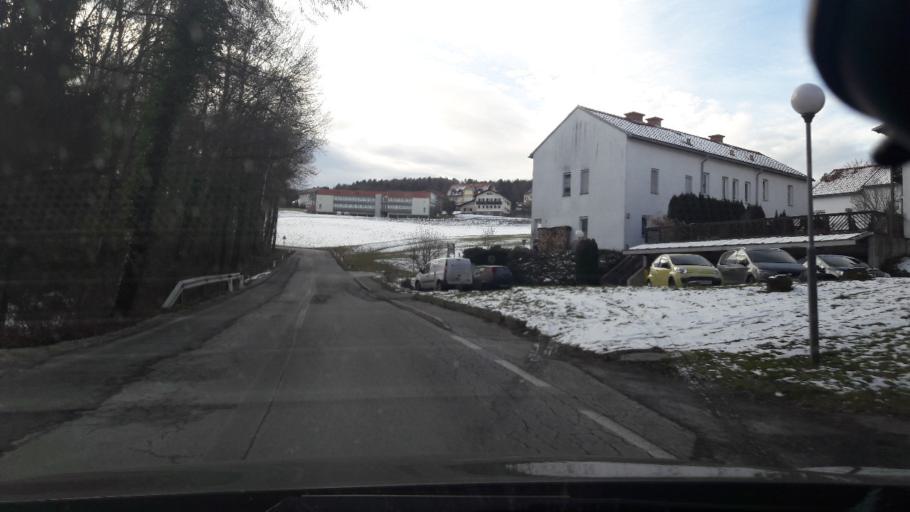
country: AT
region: Styria
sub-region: Politischer Bezirk Graz-Umgebung
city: Sankt Bartholoma
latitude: 47.0728
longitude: 15.2591
